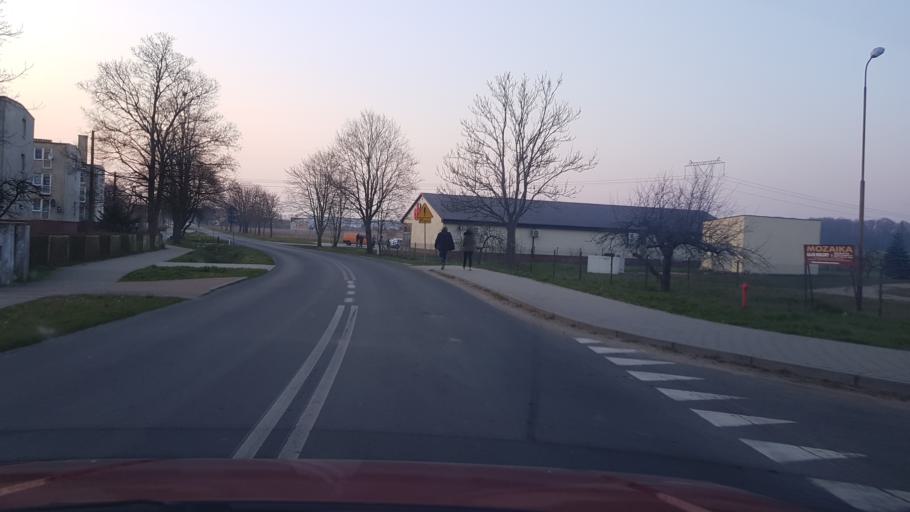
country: PL
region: West Pomeranian Voivodeship
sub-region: Powiat lobeski
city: Radowo Male
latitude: 53.6672
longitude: 15.4452
